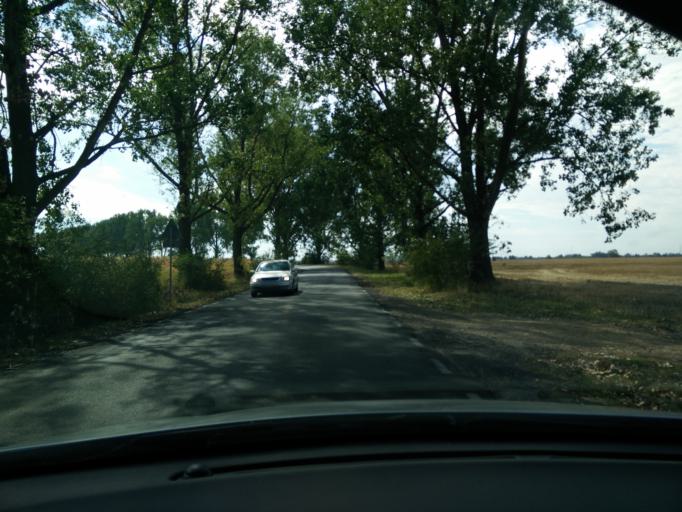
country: PL
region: Greater Poland Voivodeship
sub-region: Powiat poznanski
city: Kleszczewo
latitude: 52.2761
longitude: 17.2180
